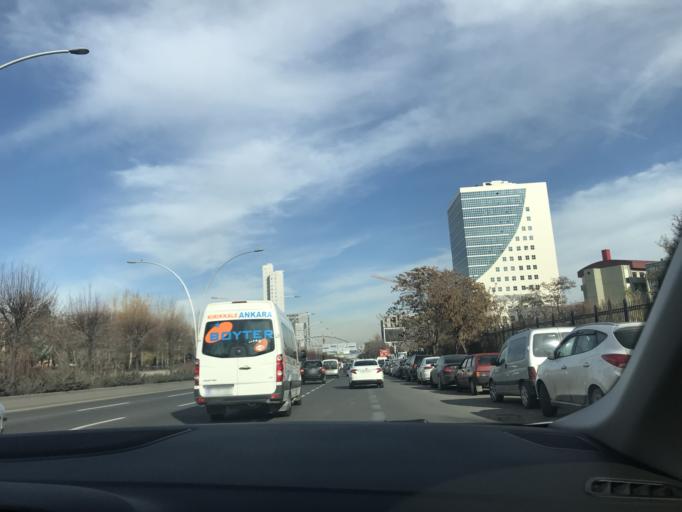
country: TR
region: Ankara
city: Ankara
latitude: 39.9332
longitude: 32.8210
